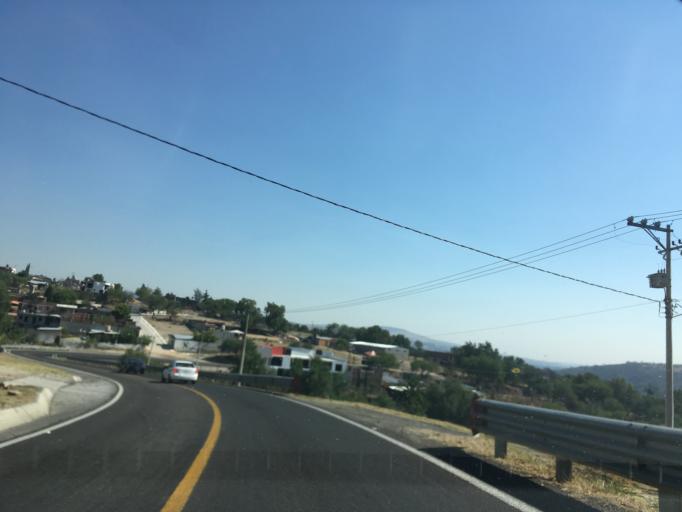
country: MX
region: Michoacan
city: Charo
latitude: 19.7494
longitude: -101.0494
